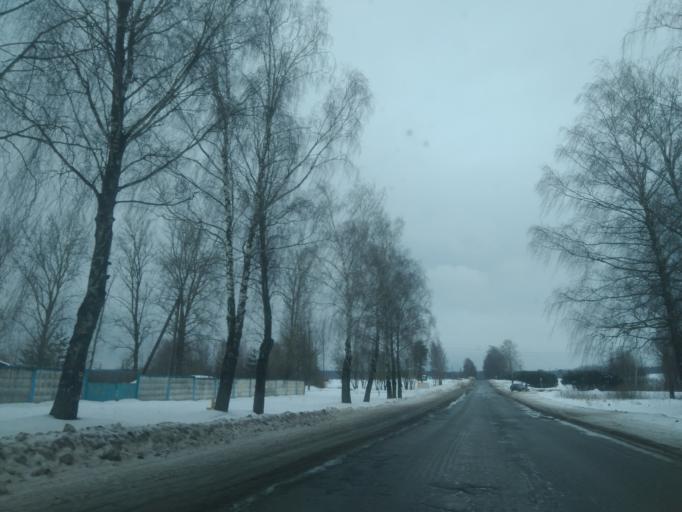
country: BY
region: Minsk
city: Ivyanyets
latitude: 53.8998
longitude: 26.7513
